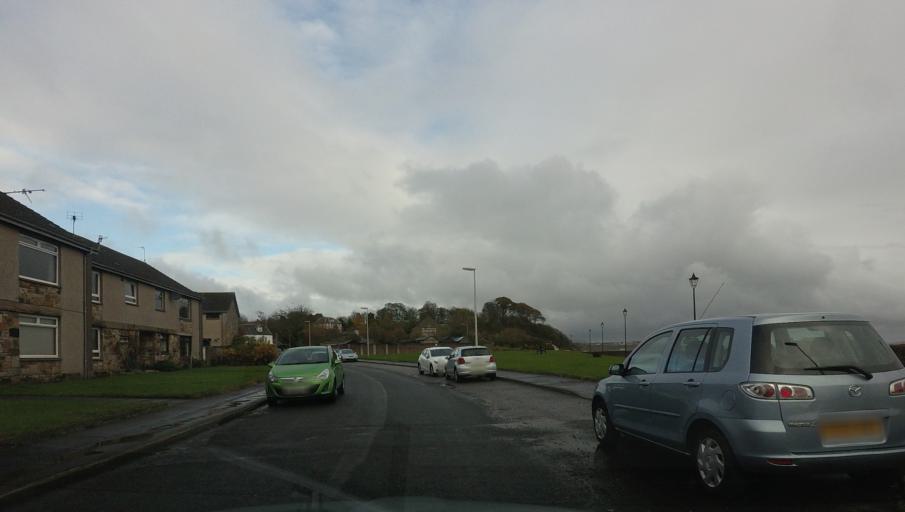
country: GB
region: Scotland
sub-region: Fife
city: East Wemyss
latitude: 56.1579
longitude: -3.0648
